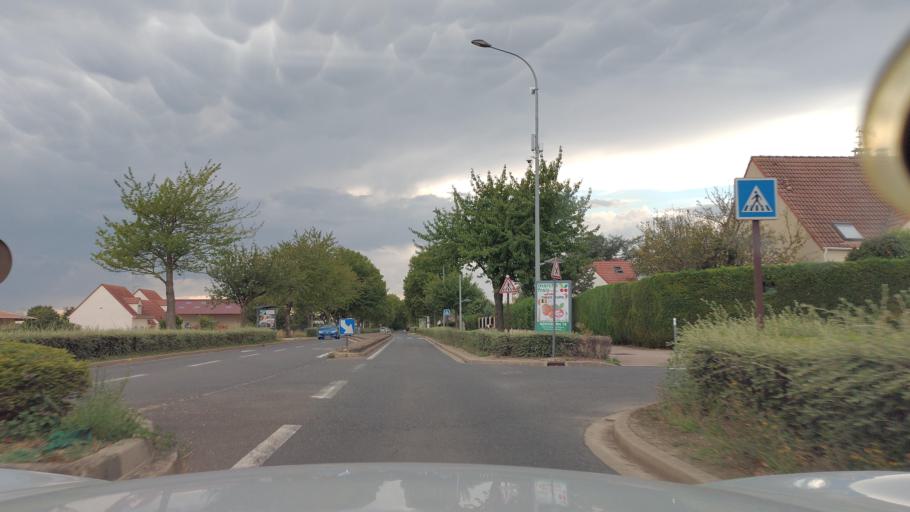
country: FR
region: Ile-de-France
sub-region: Departement de Seine-et-Marne
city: Brie-Comte-Robert
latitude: 48.6856
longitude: 2.6269
